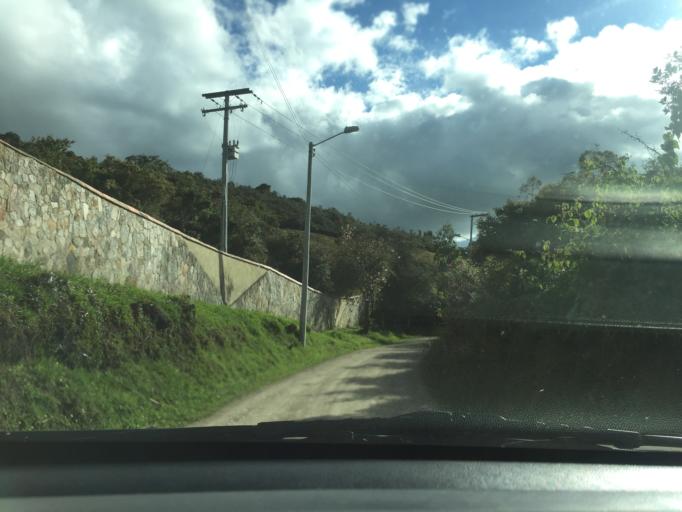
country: CO
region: Cundinamarca
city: Sopo
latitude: 4.9184
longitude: -73.9157
